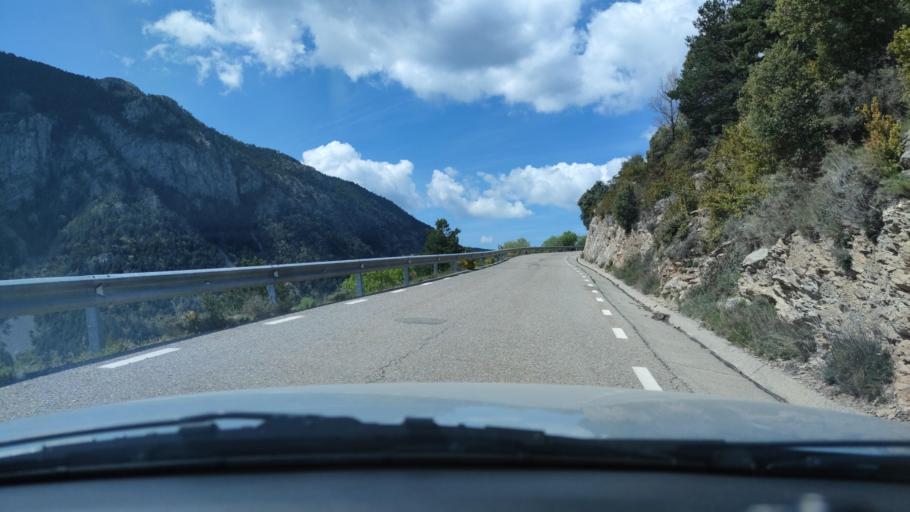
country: ES
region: Catalonia
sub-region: Provincia de Lleida
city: Coll de Nargo
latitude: 42.2906
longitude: 1.2624
